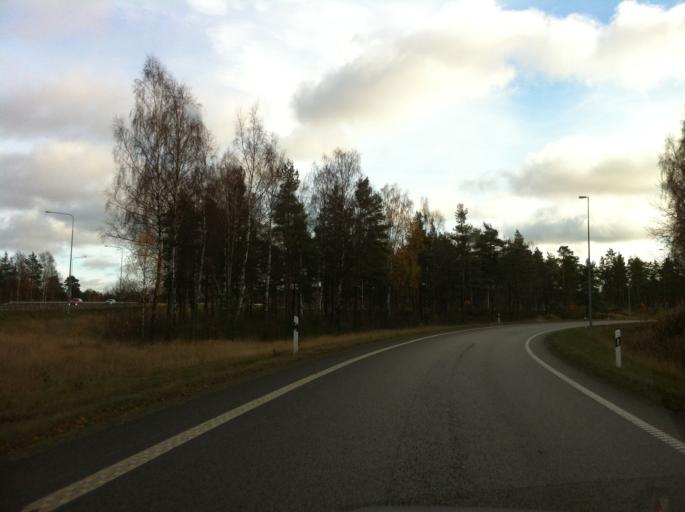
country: SE
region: Kronoberg
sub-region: Vaxjo Kommun
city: Gemla
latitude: 56.8426
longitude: 14.7116
